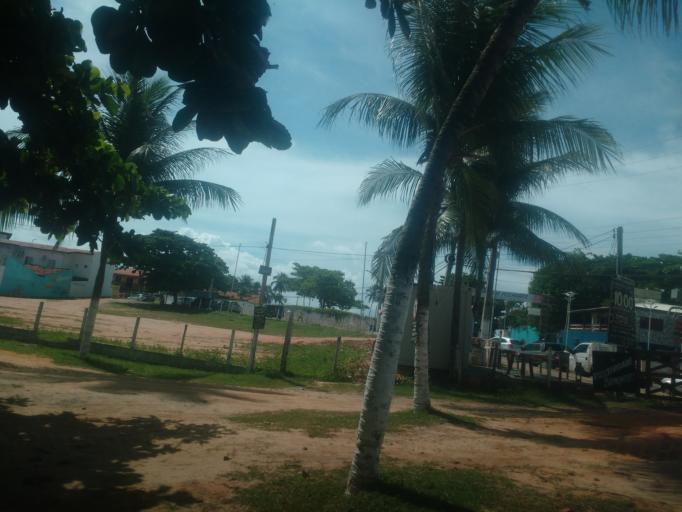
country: BR
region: Alagoas
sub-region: Marechal Deodoro
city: Marechal Deodoro
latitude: -9.7700
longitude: -35.8425
